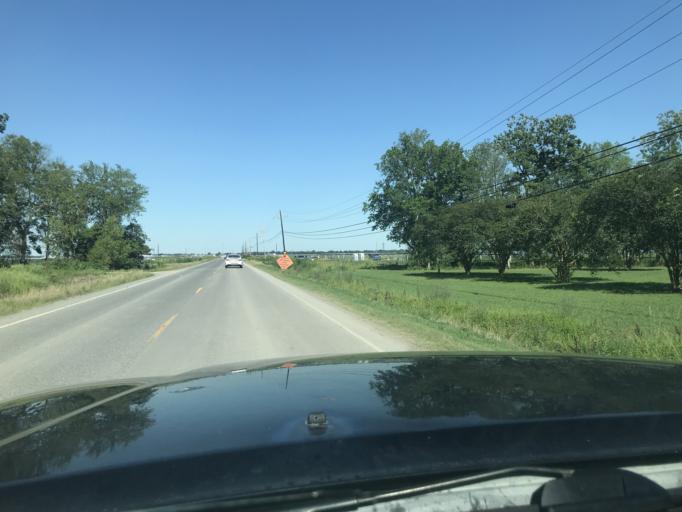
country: US
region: Louisiana
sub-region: West Baton Rouge Parish
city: Brusly
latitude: 30.4688
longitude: -91.3232
